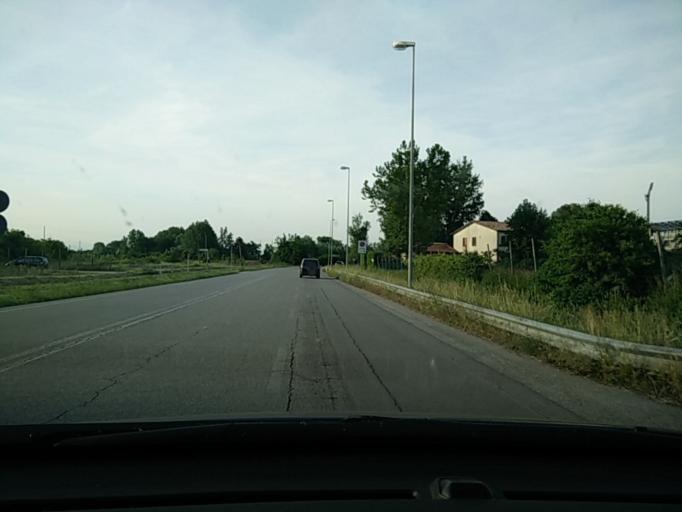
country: IT
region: Veneto
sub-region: Provincia di Padova
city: Sarmeola
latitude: 45.4300
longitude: 11.8541
